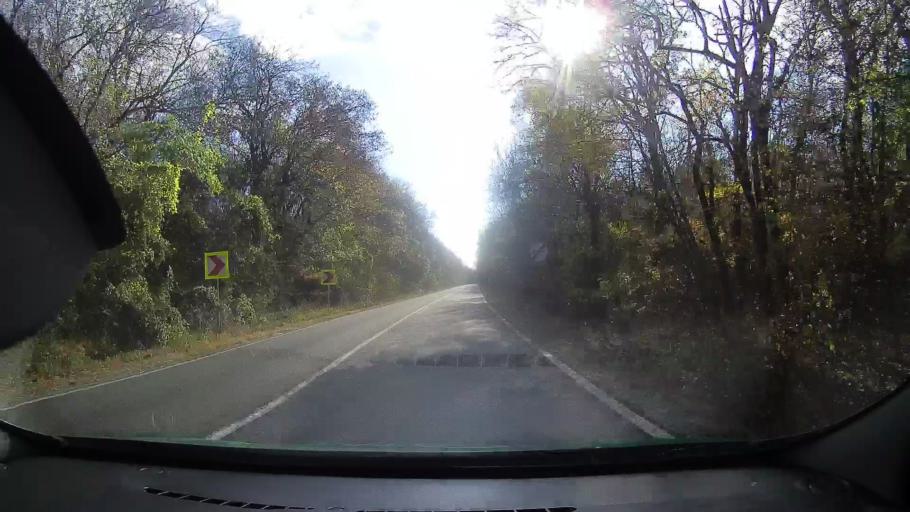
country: RO
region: Tulcea
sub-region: Oras Babadag
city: Babadag
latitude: 44.8494
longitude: 28.6978
